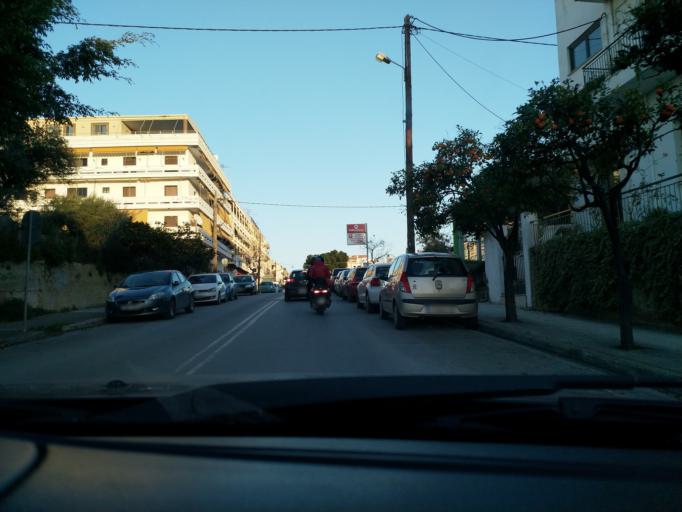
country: GR
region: Crete
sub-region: Nomos Chanias
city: Chania
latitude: 35.5100
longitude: 24.0112
